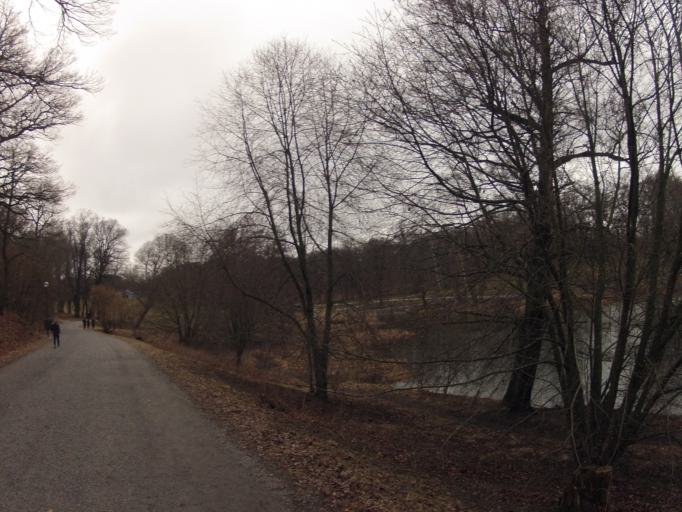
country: SE
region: Stockholm
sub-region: Norrtalje Kommun
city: Bergshamra
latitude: 59.3616
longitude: 18.0375
